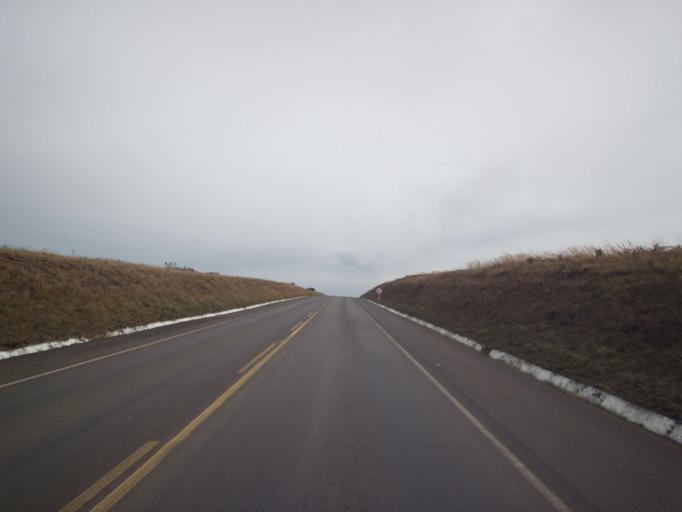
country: BR
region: Parana
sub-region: Palmas
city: Palmas
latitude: -26.7159
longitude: -51.6157
